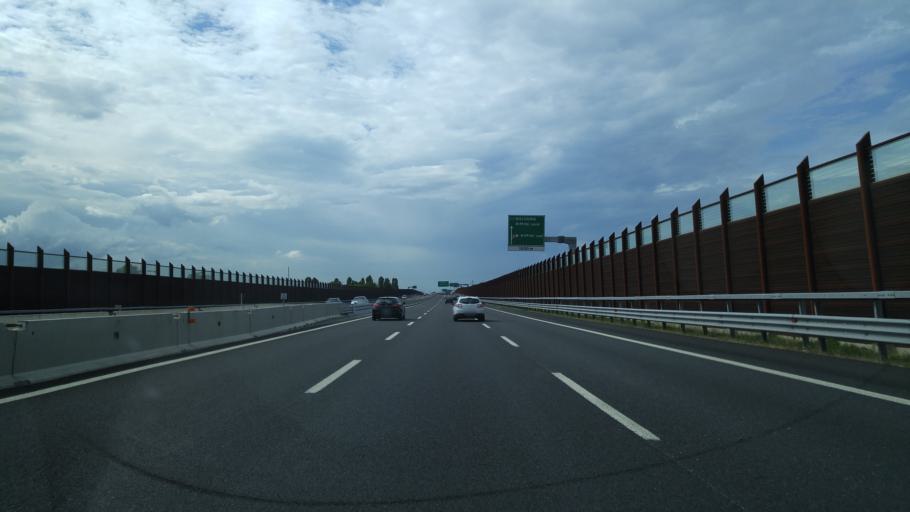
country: IT
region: Emilia-Romagna
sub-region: Provincia di Rimini
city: Rimini
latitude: 44.0285
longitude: 12.5779
